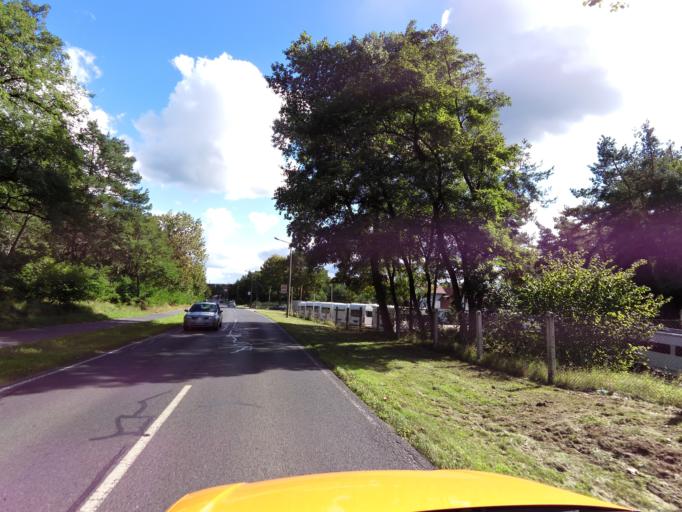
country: DE
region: Brandenburg
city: Luckenwalde
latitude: 52.0965
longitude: 13.1477
